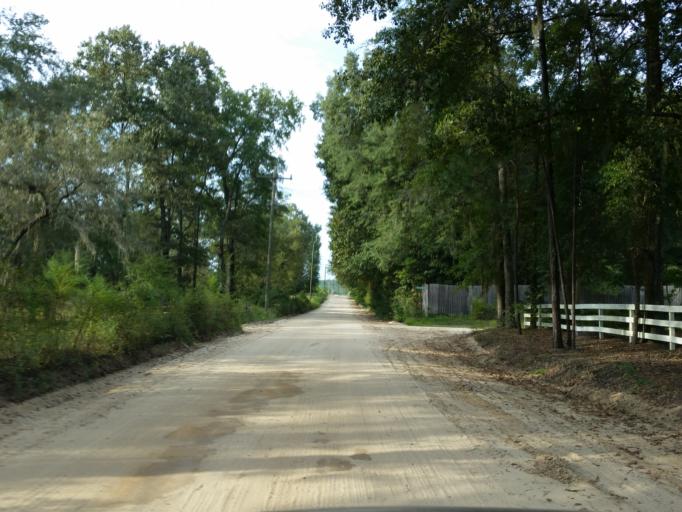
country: US
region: Florida
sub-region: Madison County
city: Madison
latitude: 30.5317
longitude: -83.2159
